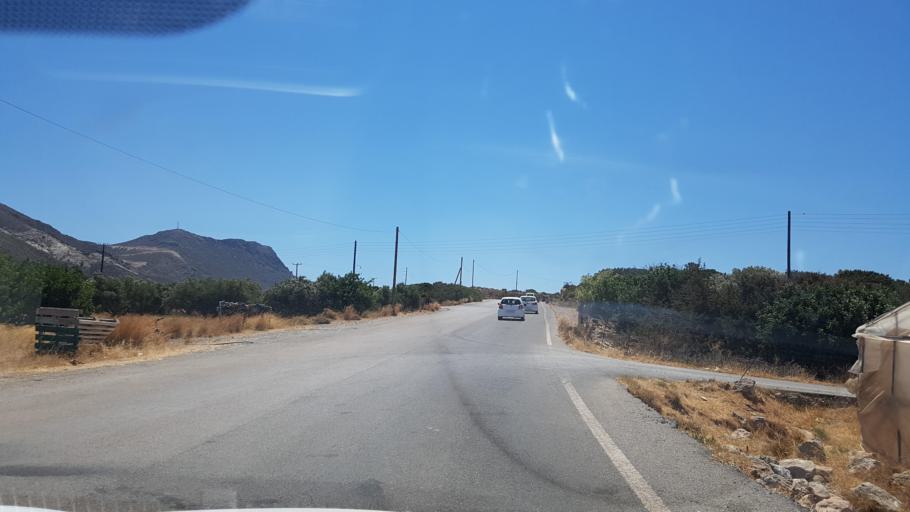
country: GR
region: Crete
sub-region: Nomos Chanias
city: Palaiochora
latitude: 35.2889
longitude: 23.5482
